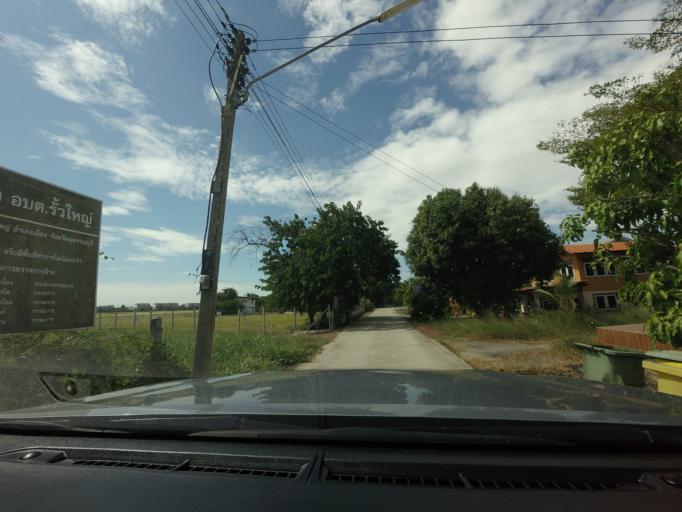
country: TH
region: Suphan Buri
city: Suphan Buri
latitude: 14.4823
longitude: 100.0878
